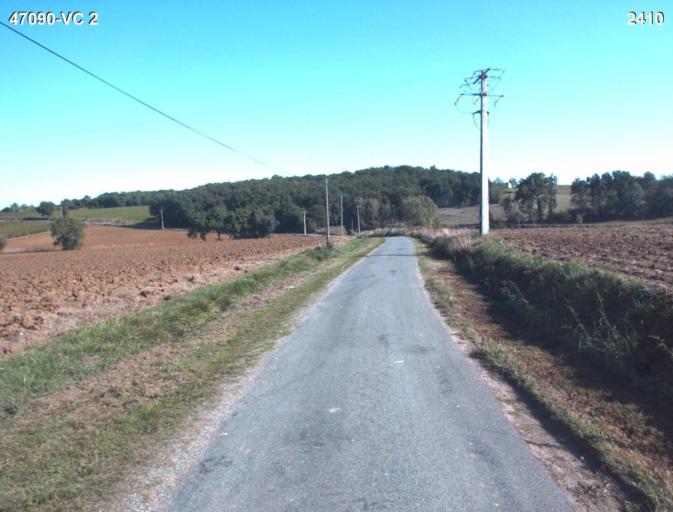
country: FR
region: Aquitaine
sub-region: Departement du Lot-et-Garonne
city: Nerac
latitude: 44.1735
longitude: 0.3761
